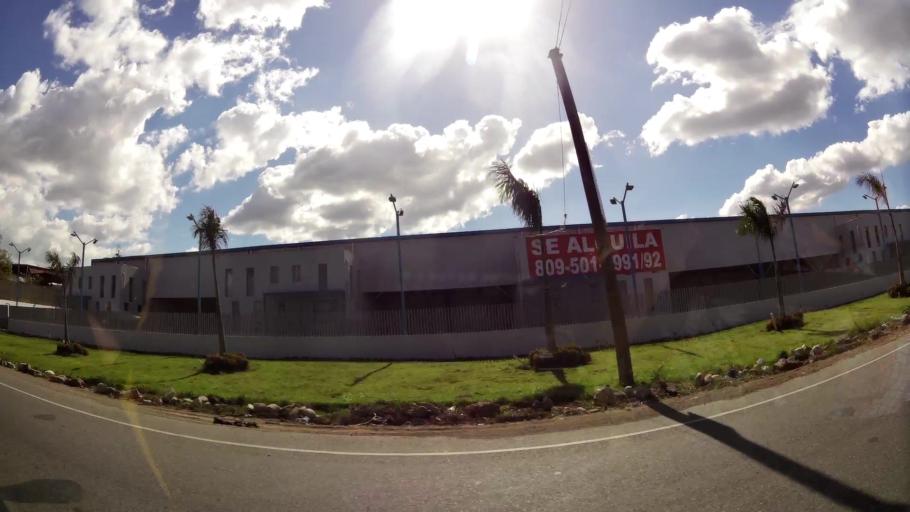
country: DO
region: Santo Domingo
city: Santo Domingo Oeste
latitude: 18.5526
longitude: -70.0551
